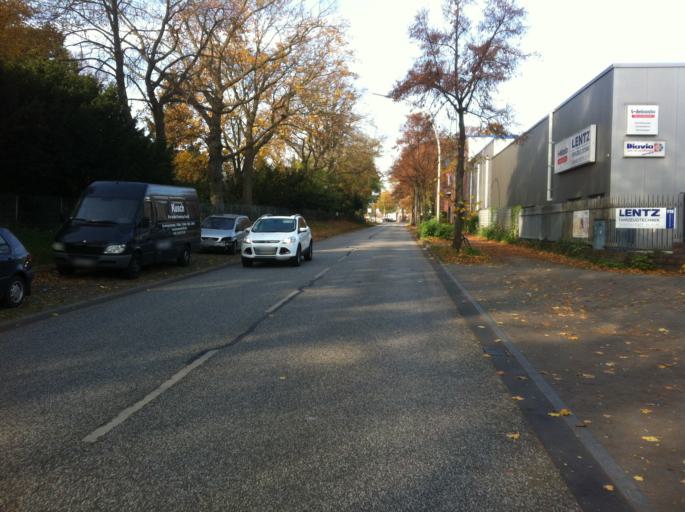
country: DE
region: Hamburg
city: Altona
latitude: 53.5654
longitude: 9.9257
